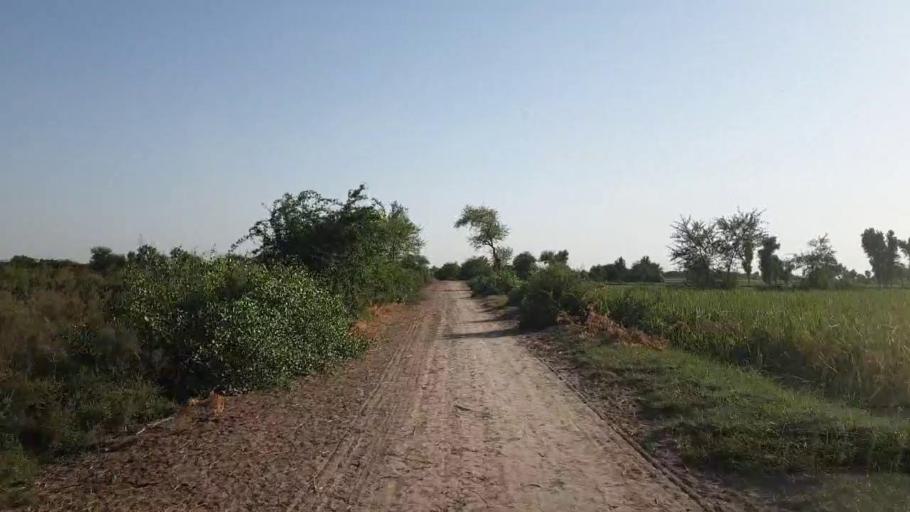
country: PK
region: Sindh
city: Badin
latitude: 24.5935
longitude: 68.9110
